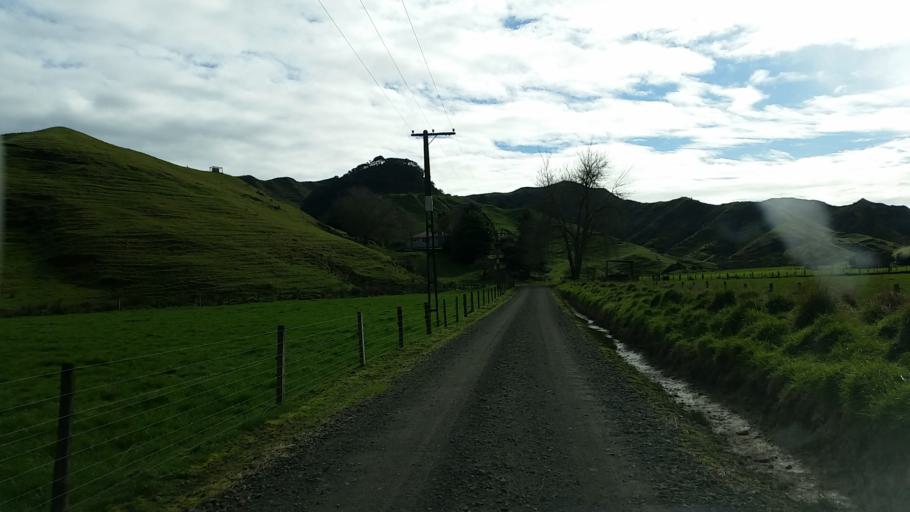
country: NZ
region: Taranaki
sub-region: South Taranaki District
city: Eltham
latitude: -39.2249
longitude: 174.5631
